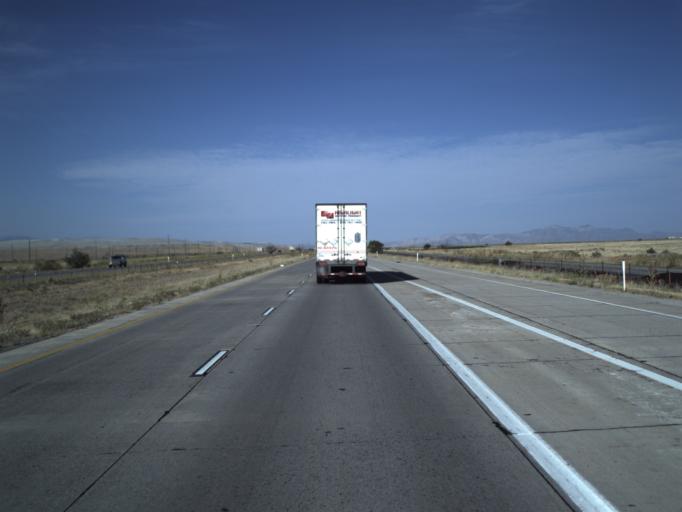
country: US
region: Utah
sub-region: Salt Lake County
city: Magna
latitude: 40.7711
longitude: -112.0707
